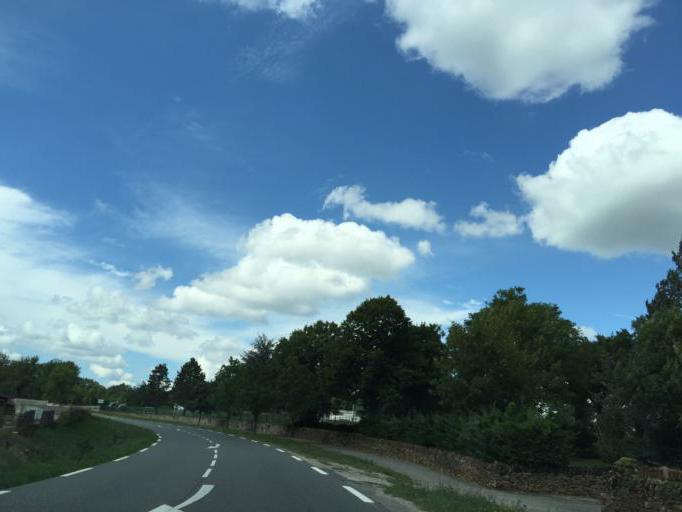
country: FR
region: Midi-Pyrenees
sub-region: Departement de l'Aveyron
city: Sebazac-Concoures
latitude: 44.3972
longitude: 2.5626
